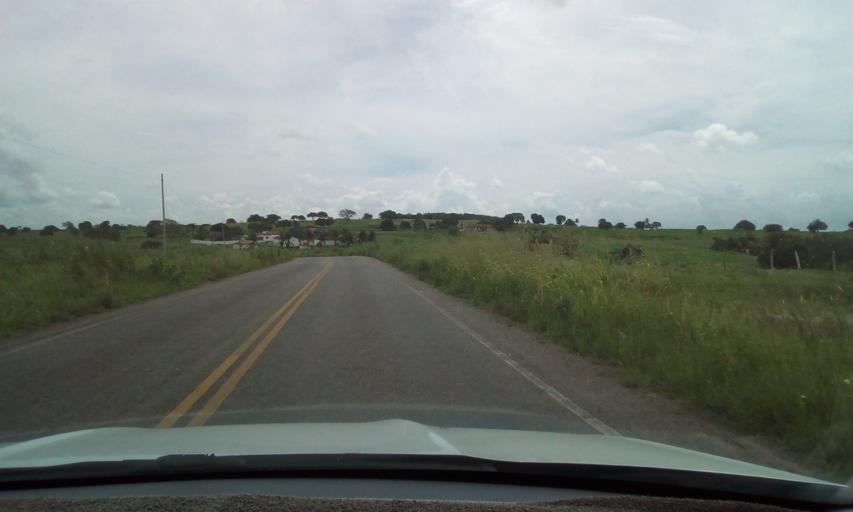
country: BR
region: Paraiba
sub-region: Gurinhem
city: Gurinhem
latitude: -7.1463
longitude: -35.3543
